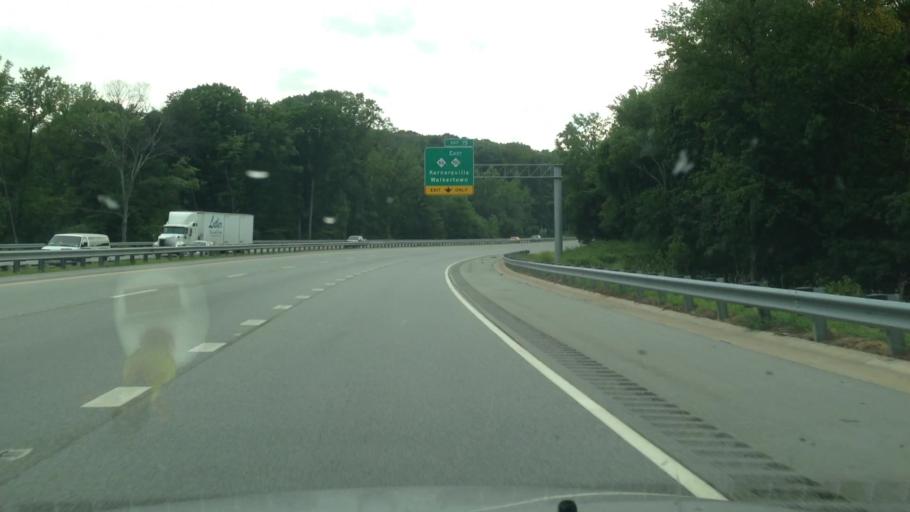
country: US
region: North Carolina
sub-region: Forsyth County
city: Kernersville
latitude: 36.1083
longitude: -80.0543
